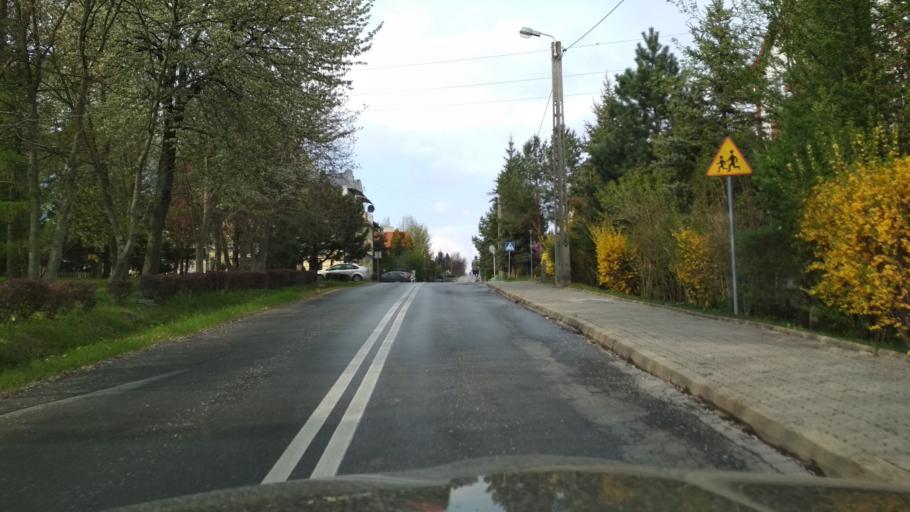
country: PL
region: Subcarpathian Voivodeship
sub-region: Rzeszow
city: Rzeszow
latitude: 50.0436
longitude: 21.9668
